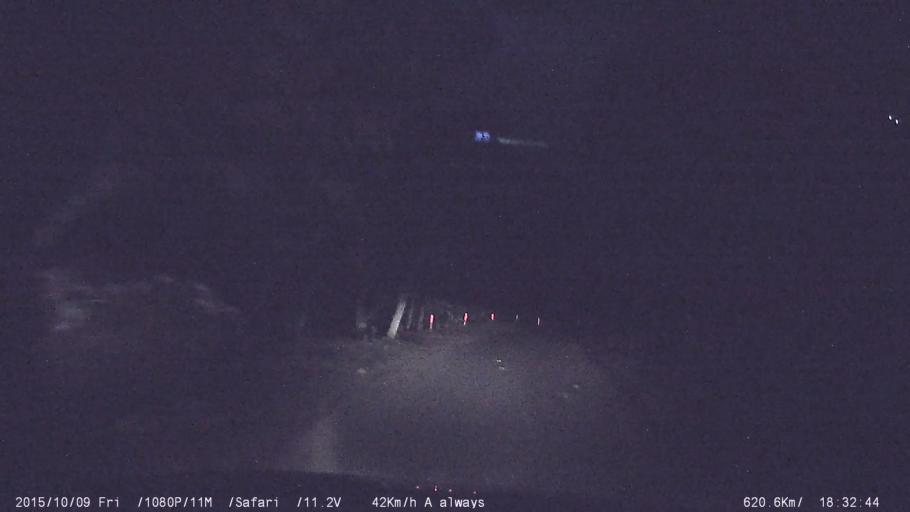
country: IN
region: Kerala
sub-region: Kottayam
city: Palackattumala
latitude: 9.7821
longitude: 76.5864
